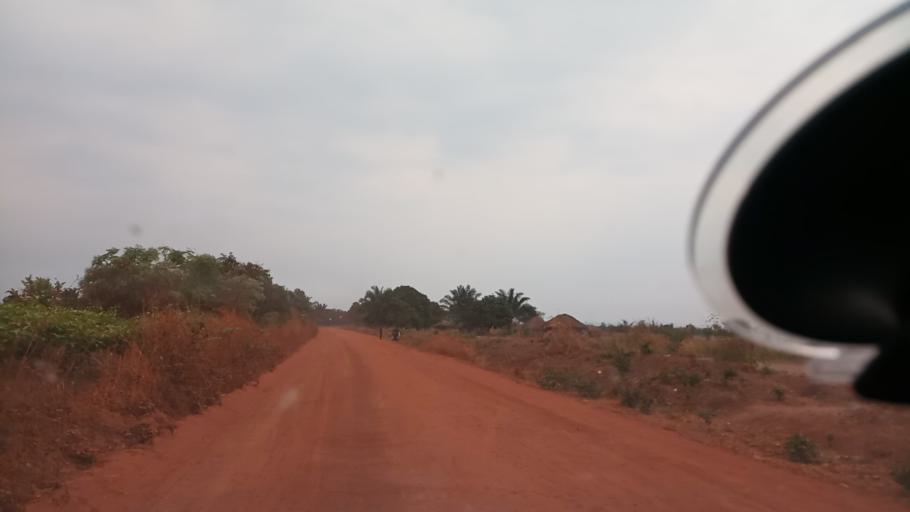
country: ZM
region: Luapula
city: Nchelenge
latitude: -9.1649
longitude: 28.2818
